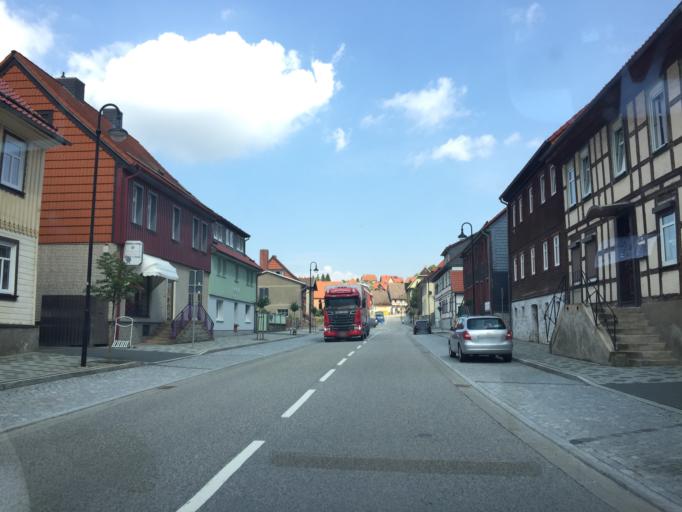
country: DE
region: Saxony-Anhalt
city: Elbingerode
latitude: 51.7710
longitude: 10.8042
